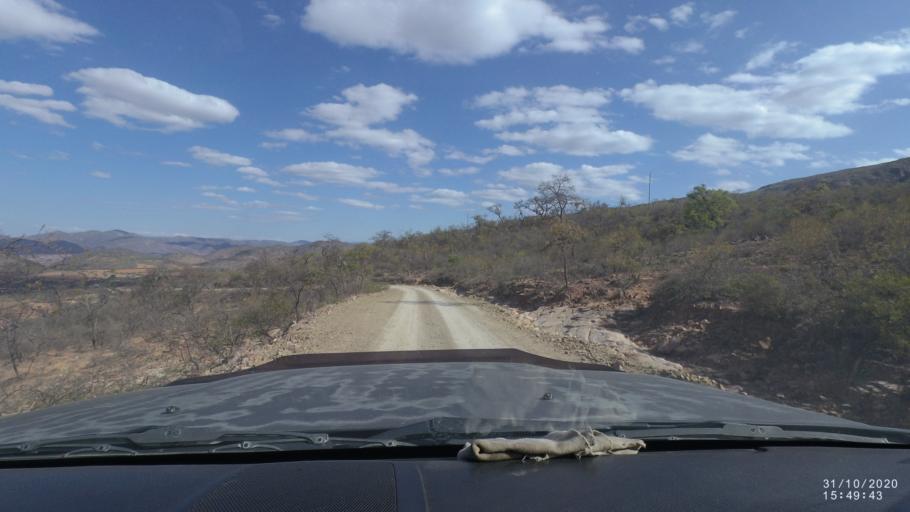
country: BO
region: Chuquisaca
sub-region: Provincia Zudanez
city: Mojocoya
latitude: -18.3129
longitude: -64.7075
